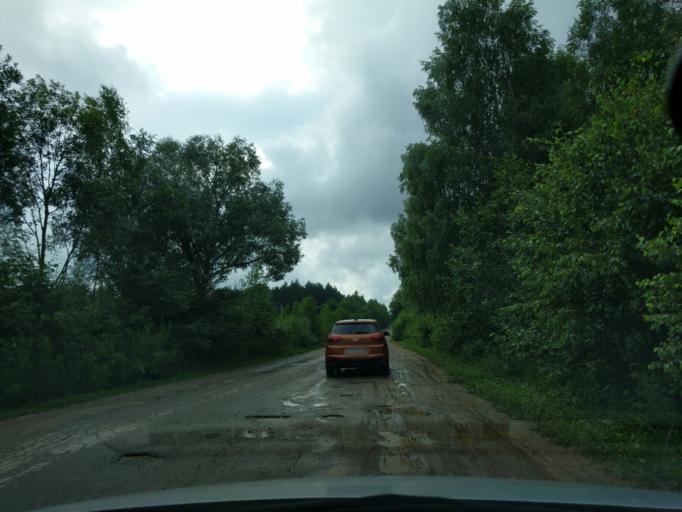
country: RU
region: Kaluga
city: Nikola-Lenivets
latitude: 54.7516
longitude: 35.6821
